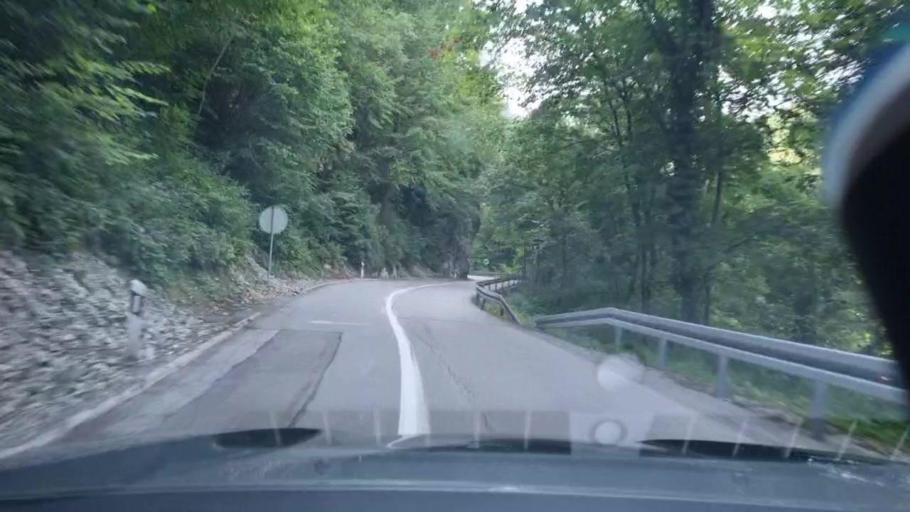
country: BA
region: Federation of Bosnia and Herzegovina
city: Stijena
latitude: 44.8825
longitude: 16.0648
